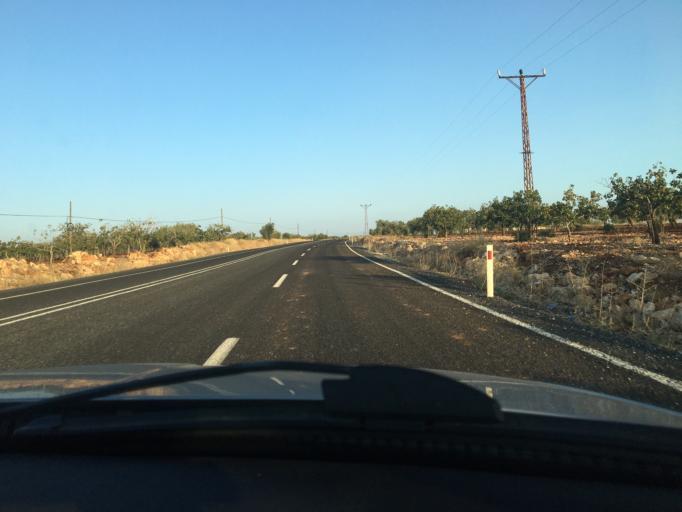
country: TR
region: Sanliurfa
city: Halfeti
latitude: 37.2442
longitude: 37.8968
